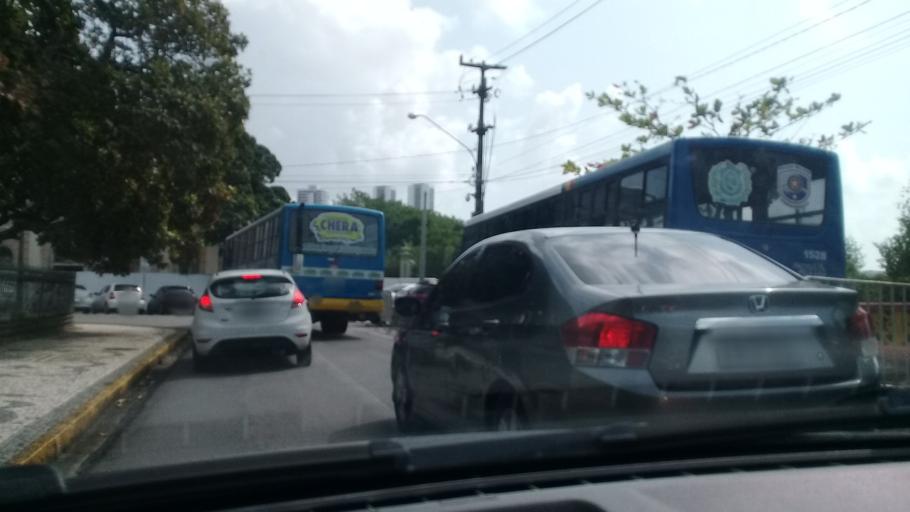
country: BR
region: Pernambuco
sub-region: Recife
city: Recife
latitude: -8.0608
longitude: -34.8766
